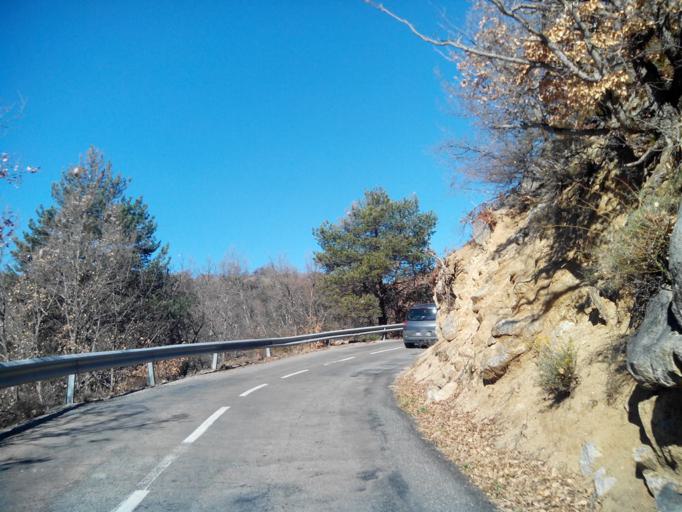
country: ES
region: Catalonia
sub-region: Provincia de Lleida
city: Lles de Cerdanya
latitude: 42.3717
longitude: 1.6834
